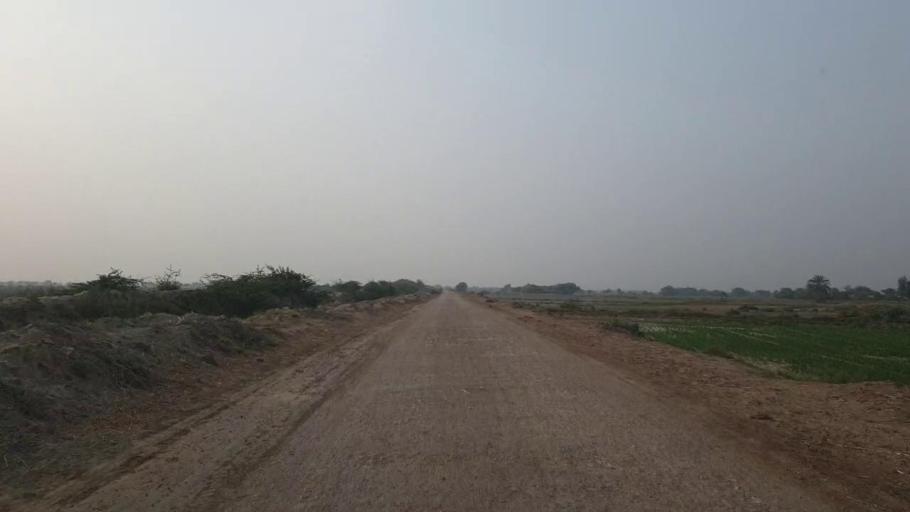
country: PK
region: Sindh
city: Mirpur Batoro
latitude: 24.6422
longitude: 68.3958
